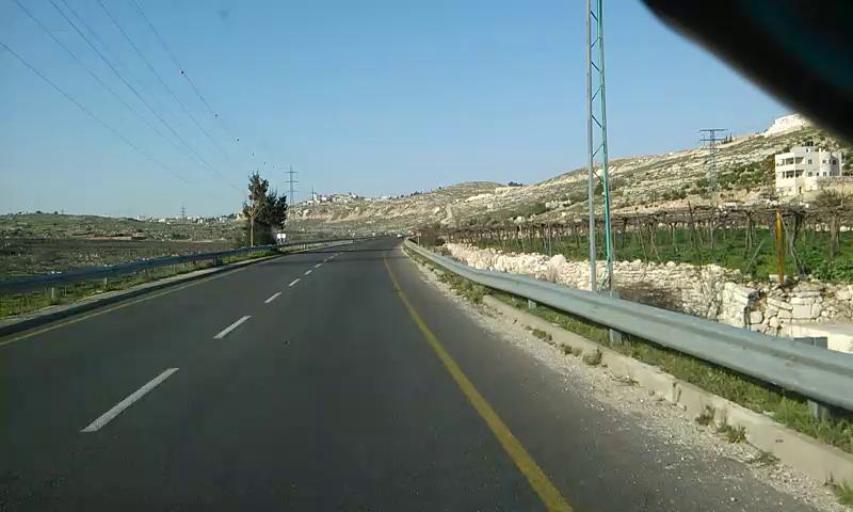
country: PS
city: Al Buq`ah
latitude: 31.5496
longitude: 35.1344
